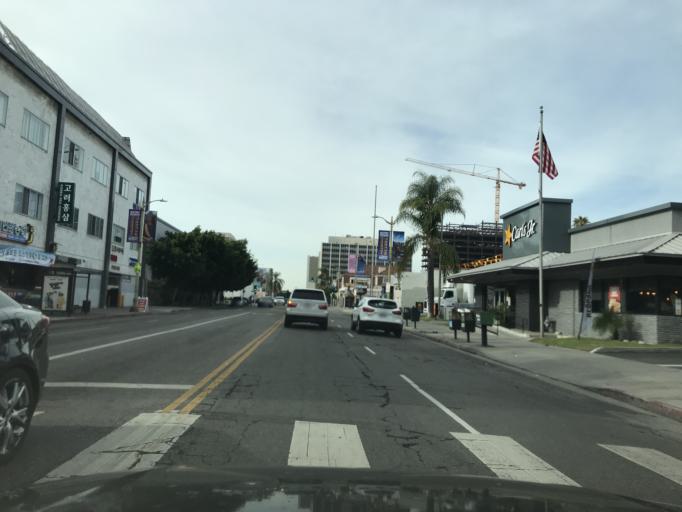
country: US
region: California
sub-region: Los Angeles County
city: Silver Lake
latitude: 34.0637
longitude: -118.2872
